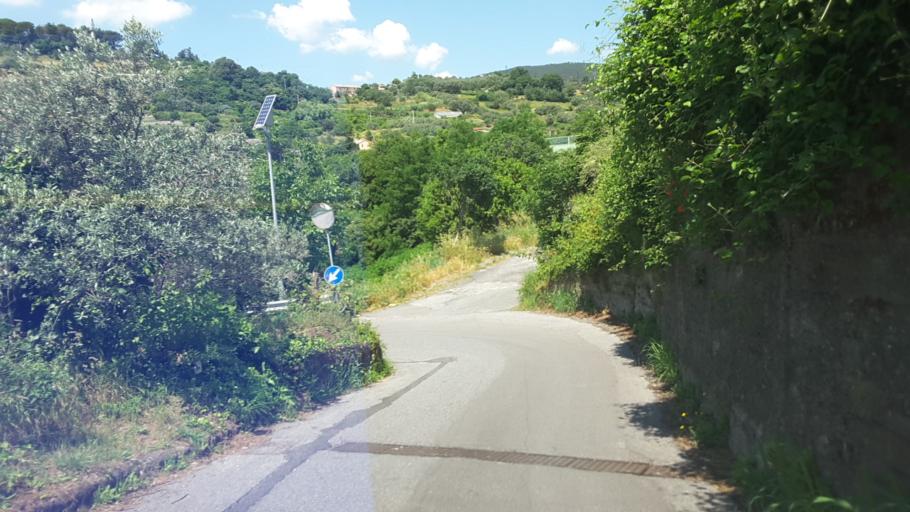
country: IT
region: Liguria
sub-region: Provincia di Genova
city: Mele
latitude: 44.4316
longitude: 8.7885
